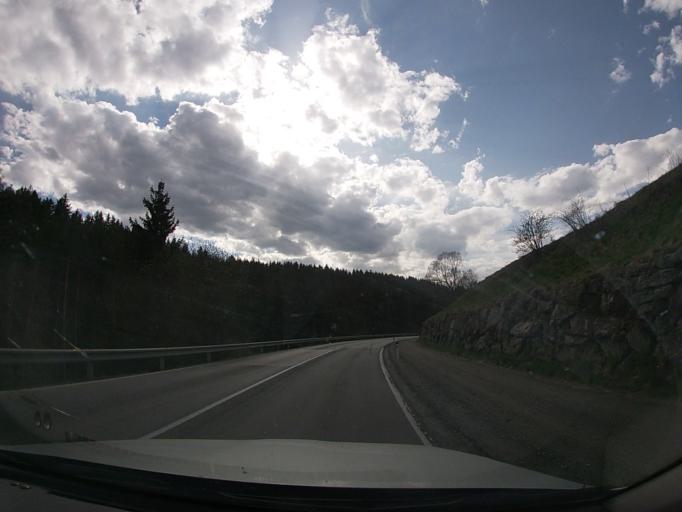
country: AT
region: Styria
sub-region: Politischer Bezirk Murau
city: Perchau am Sattel
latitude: 47.0905
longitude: 14.4385
